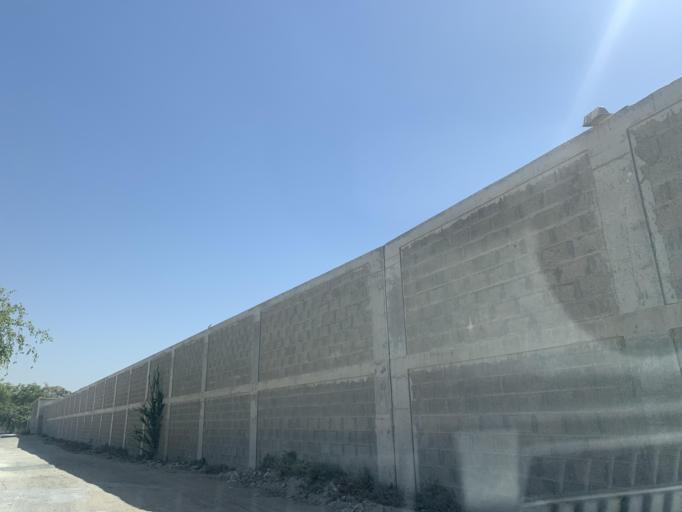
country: BH
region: Manama
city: Jidd Hafs
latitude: 26.2296
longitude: 50.4980
